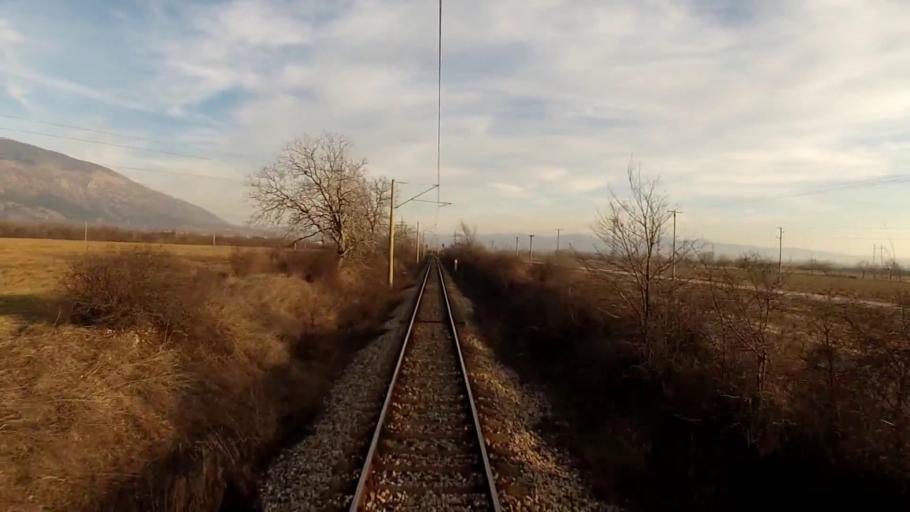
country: BG
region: Plovdiv
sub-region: Obshtina Karlovo
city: Karlovo
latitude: 42.6325
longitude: 24.7759
